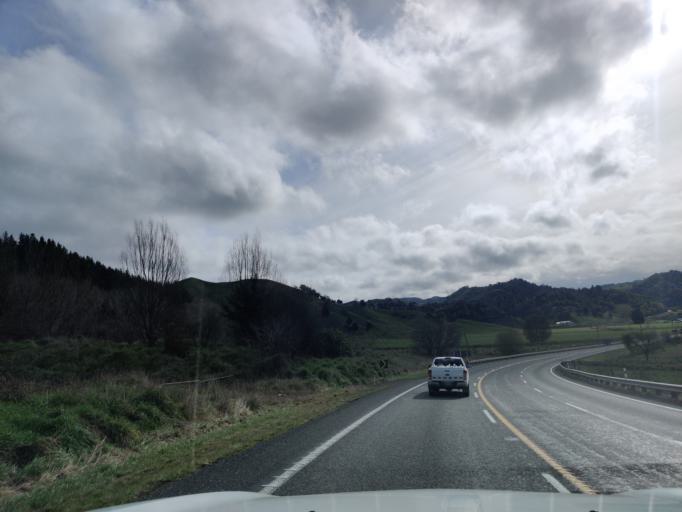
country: NZ
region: Manawatu-Wanganui
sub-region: Ruapehu District
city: Waiouru
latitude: -39.8232
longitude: 175.7762
